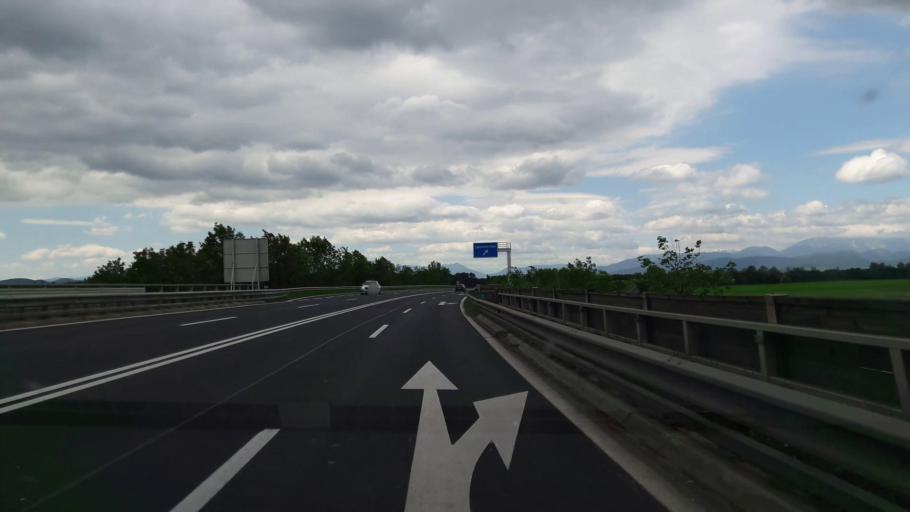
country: AT
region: Lower Austria
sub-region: Wiener Neustadt Stadt
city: Wiener Neustadt
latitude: 47.7852
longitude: 16.2489
